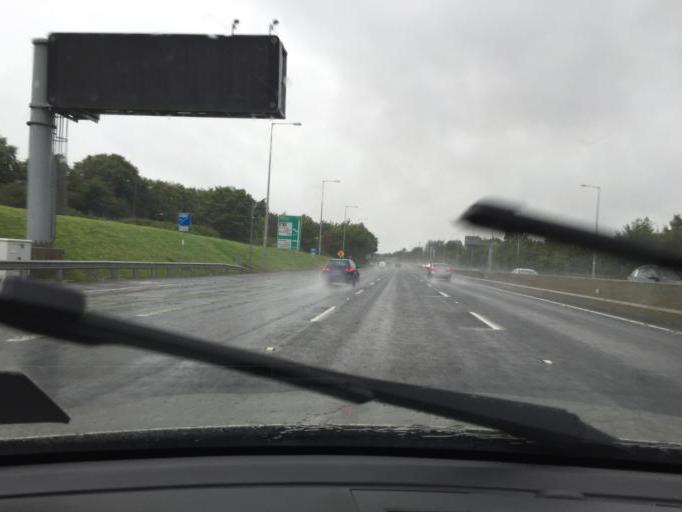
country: IE
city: Palmerstown
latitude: 53.3574
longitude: -6.4051
